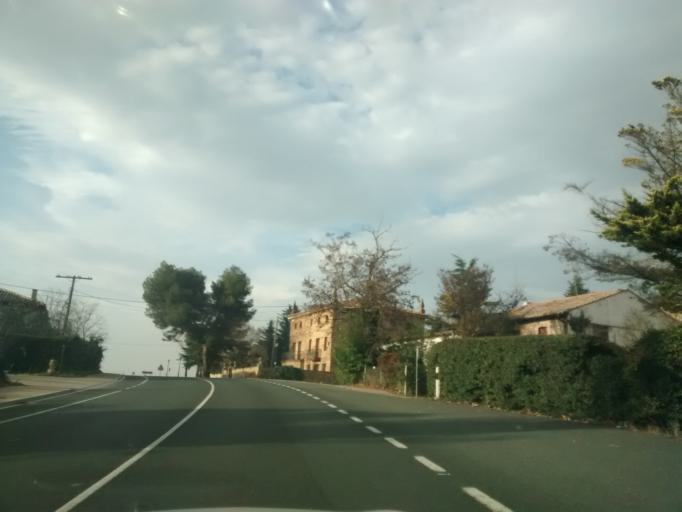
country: ES
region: La Rioja
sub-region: Provincia de La Rioja
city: Torremontalbo
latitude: 42.5009
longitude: -2.6848
